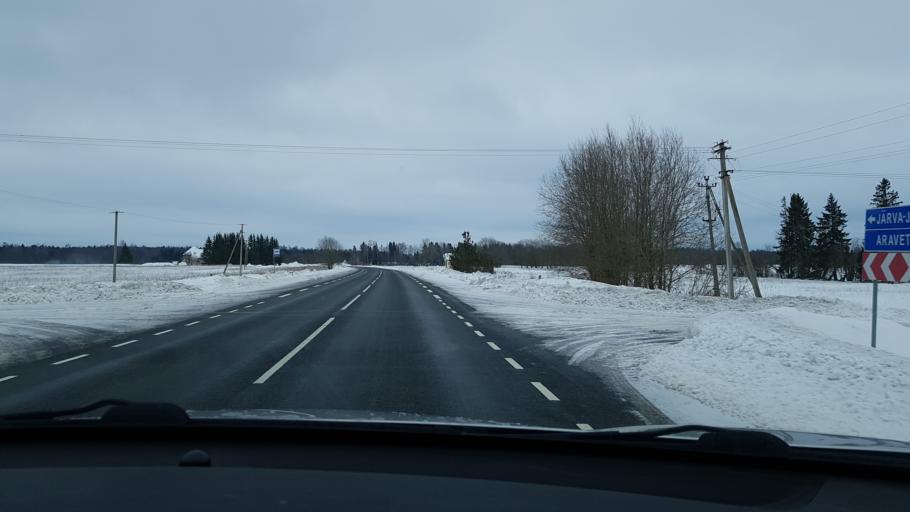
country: EE
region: Jaervamaa
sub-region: Jaerva-Jaani vald
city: Jarva-Jaani
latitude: 59.0836
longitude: 25.8400
